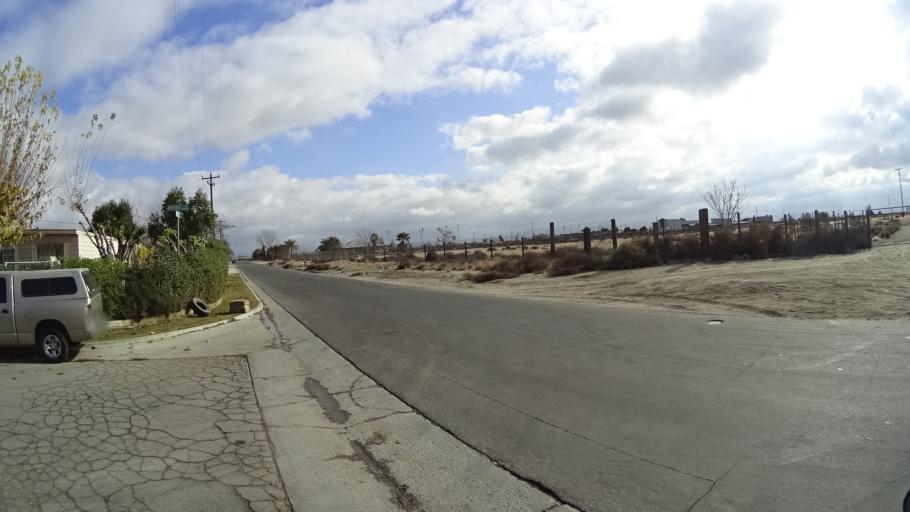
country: US
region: California
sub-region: Kern County
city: Greenfield
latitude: 35.3214
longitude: -118.9888
